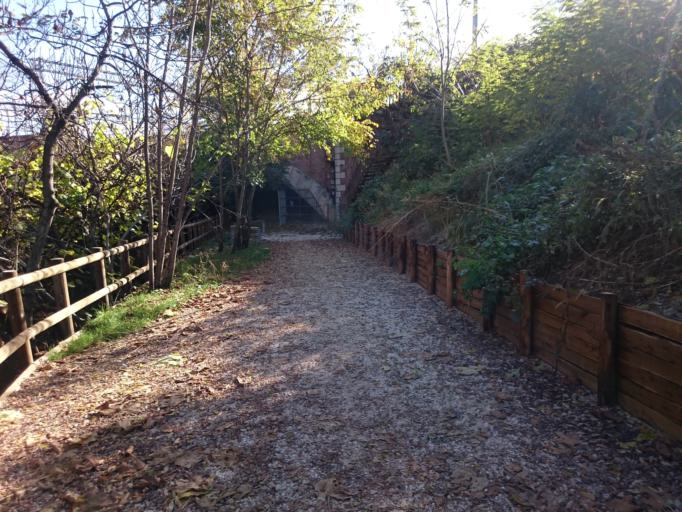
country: IT
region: Emilia-Romagna
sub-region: Provincia di Bologna
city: Bologna
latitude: 44.5081
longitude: 11.3322
